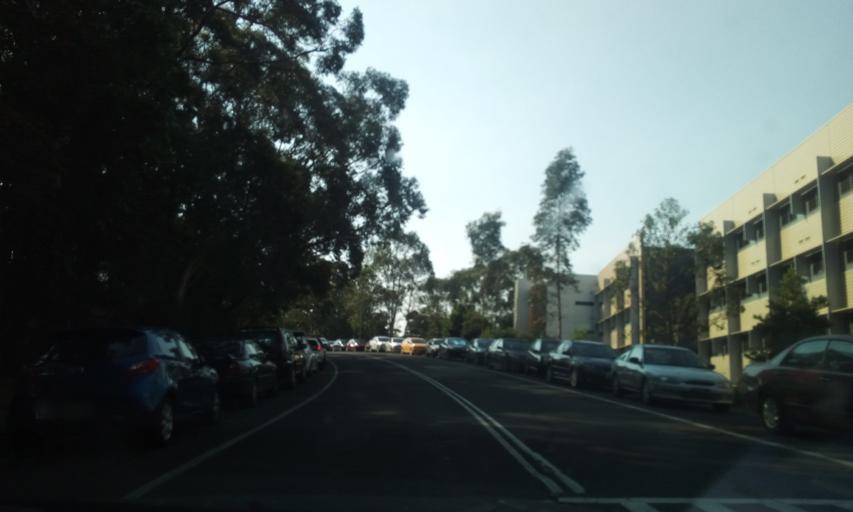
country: AU
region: New South Wales
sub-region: Wollongong
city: Mount Ousley
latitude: -34.4062
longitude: 150.8724
